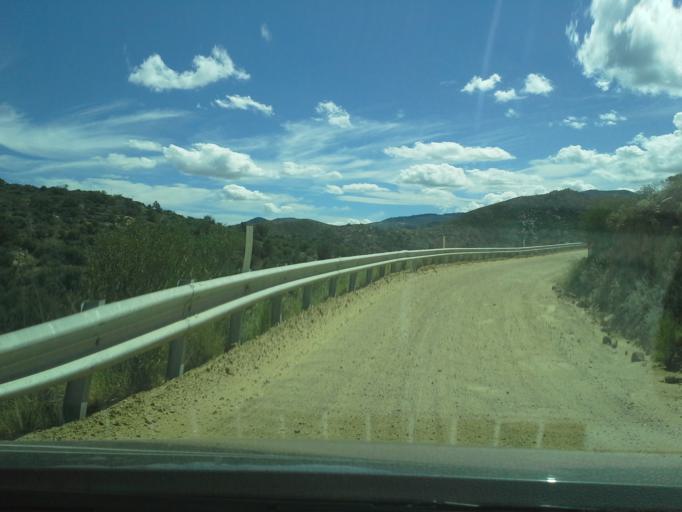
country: US
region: Arizona
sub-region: Yavapai County
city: Mayer
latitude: 34.2352
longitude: -112.3026
